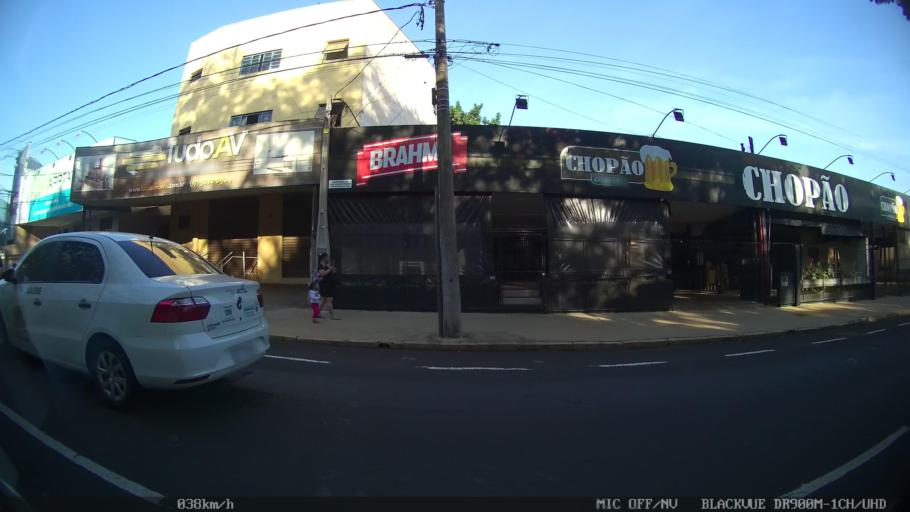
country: BR
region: Sao Paulo
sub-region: Sao Jose Do Rio Preto
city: Sao Jose do Rio Preto
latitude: -20.8142
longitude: -49.3671
